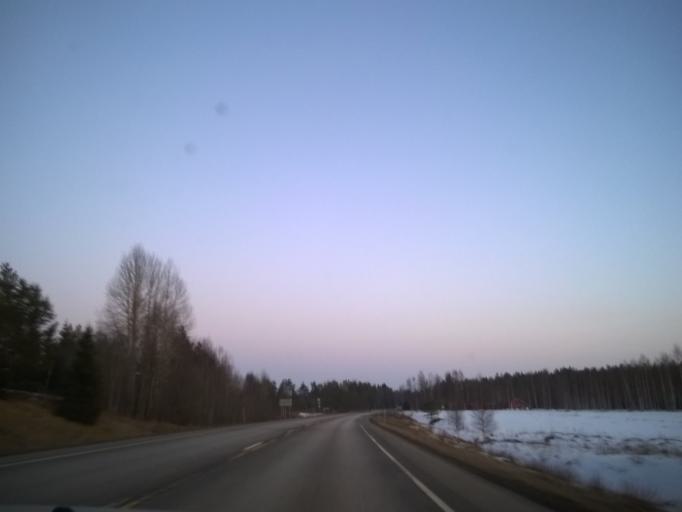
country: FI
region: Northern Ostrobothnia
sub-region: Nivala-Haapajaervi
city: Pyhaejaervi
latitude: 63.8104
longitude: 25.9085
